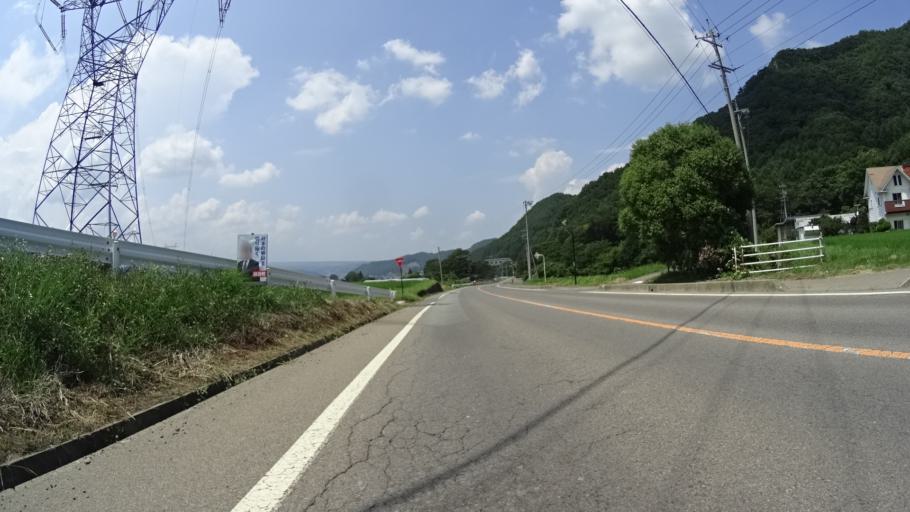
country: JP
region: Nagano
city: Saku
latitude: 36.1437
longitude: 138.5183
